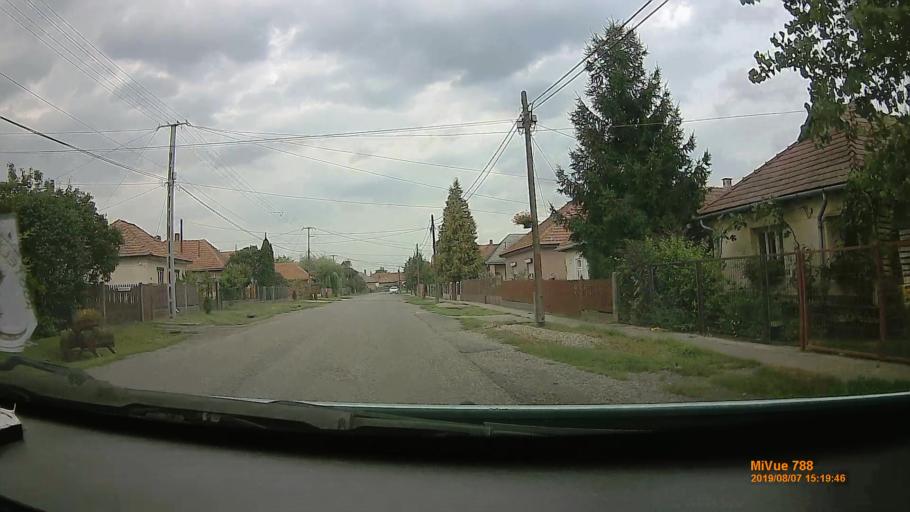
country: HU
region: Borsod-Abauj-Zemplen
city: Encs
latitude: 48.3518
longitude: 21.1441
